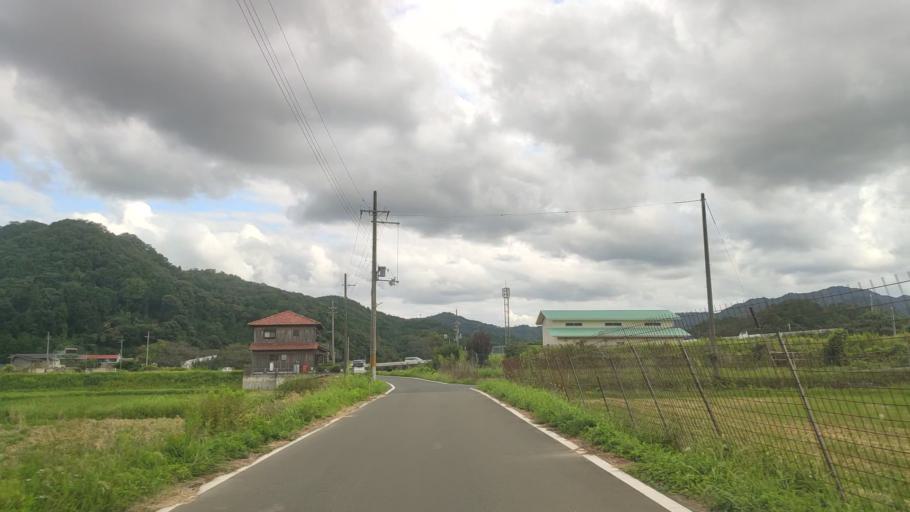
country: JP
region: Hyogo
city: Toyooka
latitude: 35.5976
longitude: 134.8850
